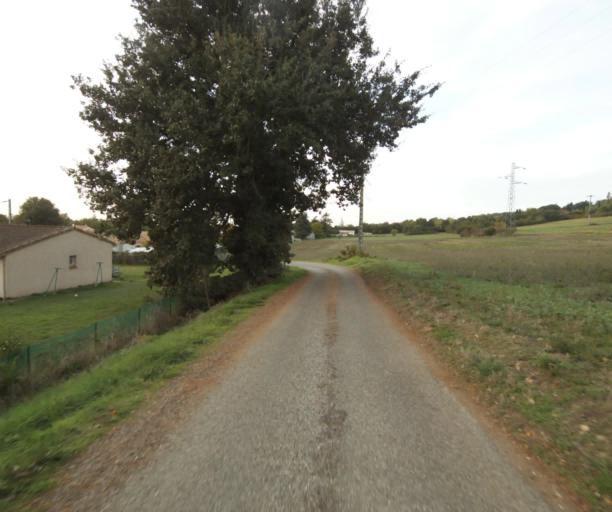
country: FR
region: Midi-Pyrenees
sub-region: Departement du Tarn-et-Garonne
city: Pompignan
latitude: 43.8220
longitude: 1.3084
